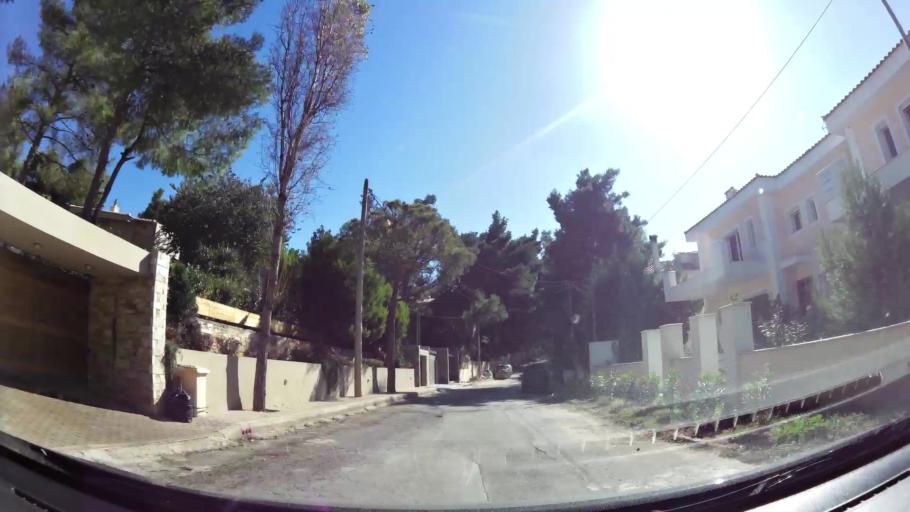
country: GR
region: Attica
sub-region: Nomarchia Anatolikis Attikis
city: Rodopoli
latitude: 38.1098
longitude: 23.8745
